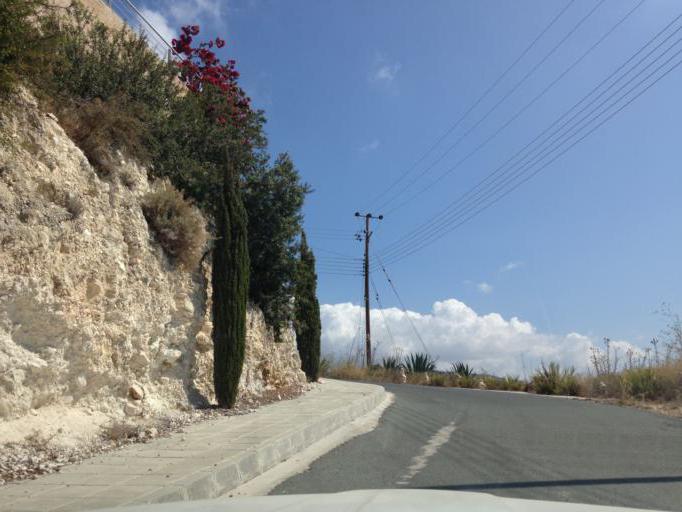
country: CY
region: Pafos
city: Pegeia
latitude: 34.8887
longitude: 32.3875
